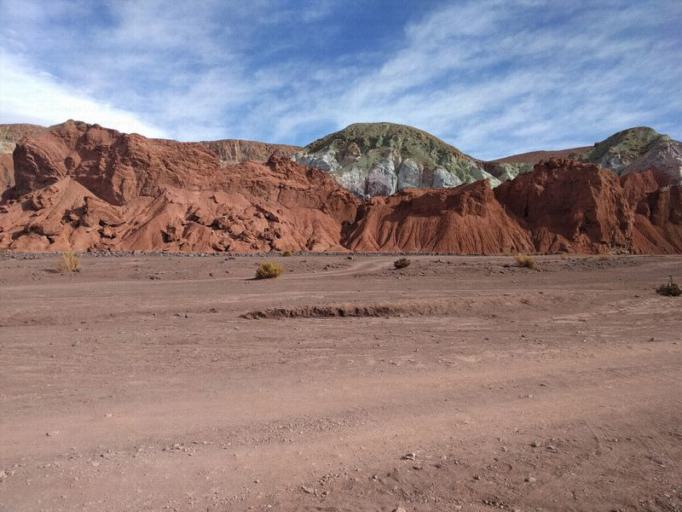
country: CL
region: Antofagasta
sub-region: Provincia de El Loa
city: San Pedro de Atacama
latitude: -22.6412
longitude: -68.2413
